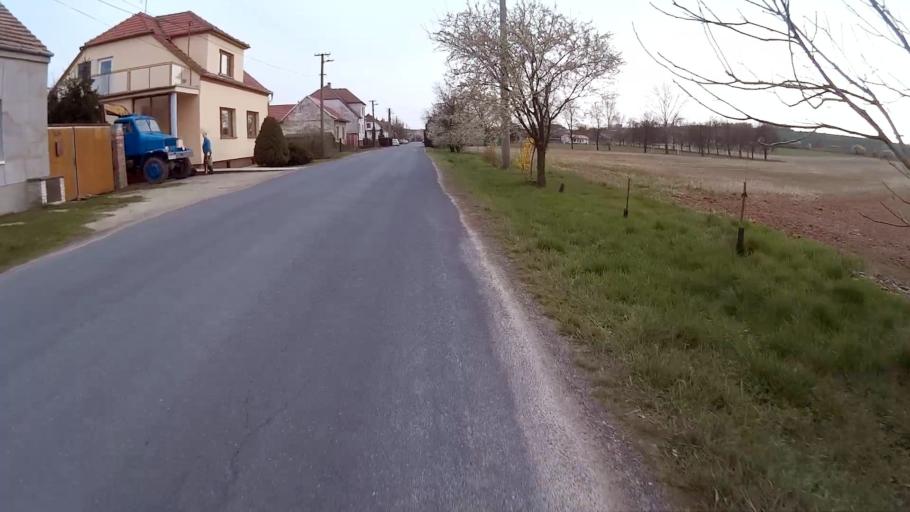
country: CZ
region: South Moravian
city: Ivancice
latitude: 49.0757
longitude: 16.3484
